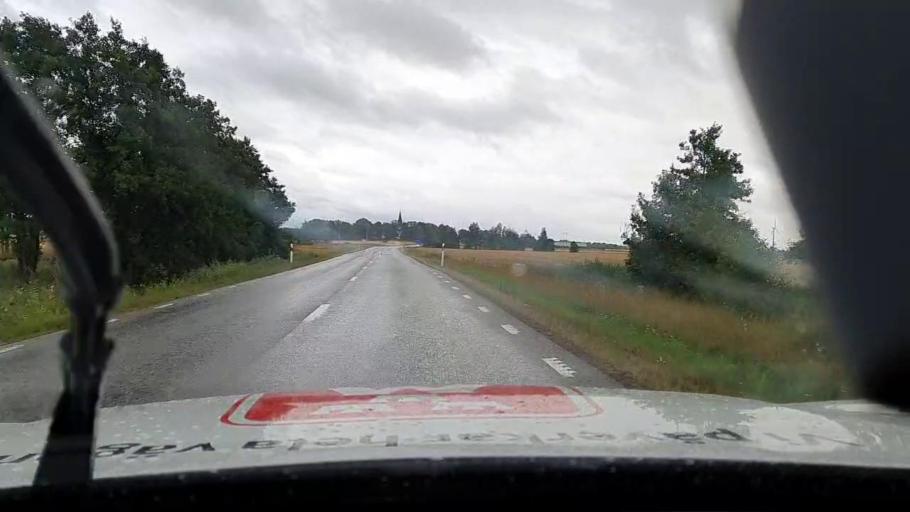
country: SE
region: Vaestra Goetaland
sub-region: Toreboda Kommun
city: Toereboda
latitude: 58.6147
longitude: 14.0108
